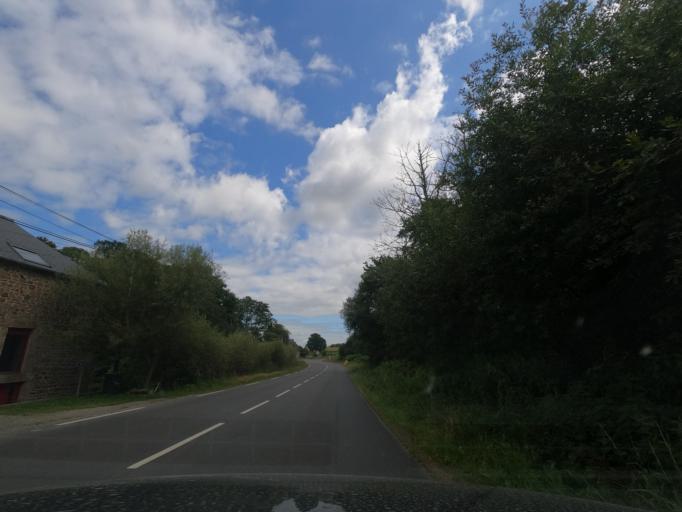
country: FR
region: Pays de la Loire
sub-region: Departement de la Mayenne
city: Landivy
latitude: 48.4436
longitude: -1.0798
